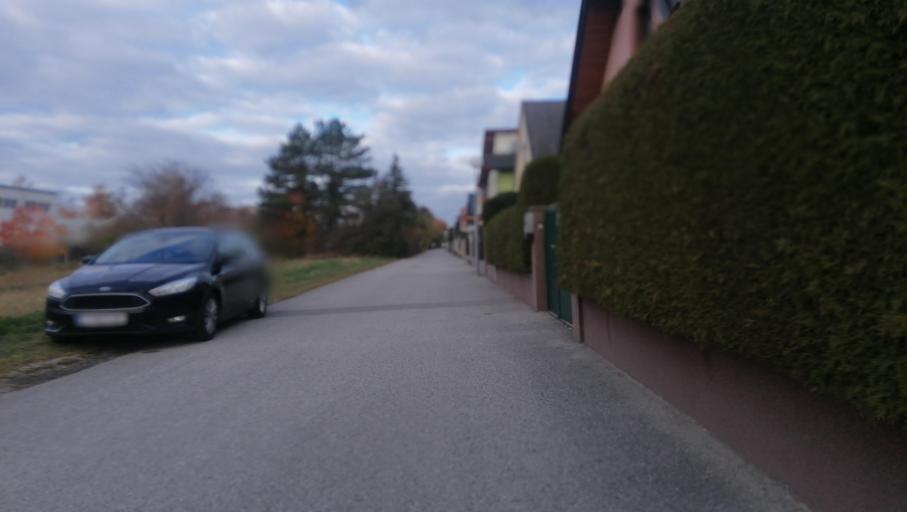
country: AT
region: Lower Austria
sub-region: Politischer Bezirk Baden
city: Oberwaltersdorf
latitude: 47.9762
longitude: 16.3270
